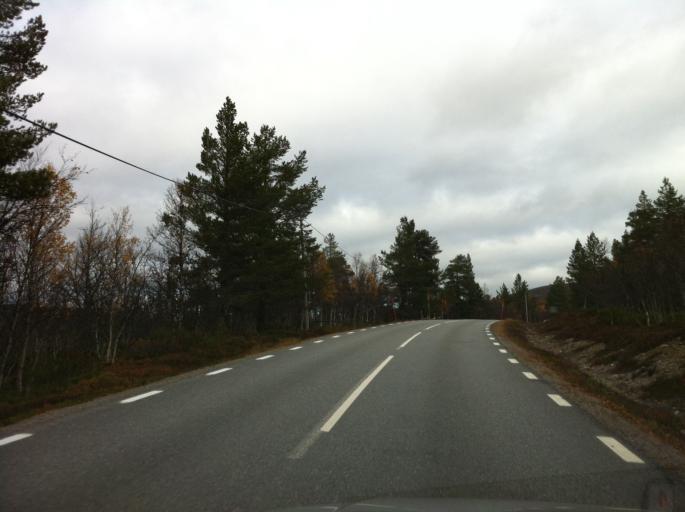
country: NO
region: Hedmark
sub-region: Engerdal
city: Engerdal
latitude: 62.0869
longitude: 12.3078
